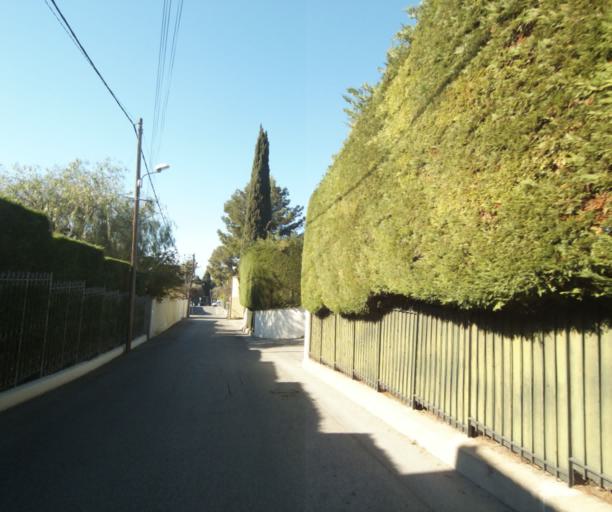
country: FR
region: Provence-Alpes-Cote d'Azur
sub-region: Departement des Alpes-Maritimes
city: Antibes
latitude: 43.5550
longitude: 7.1267
